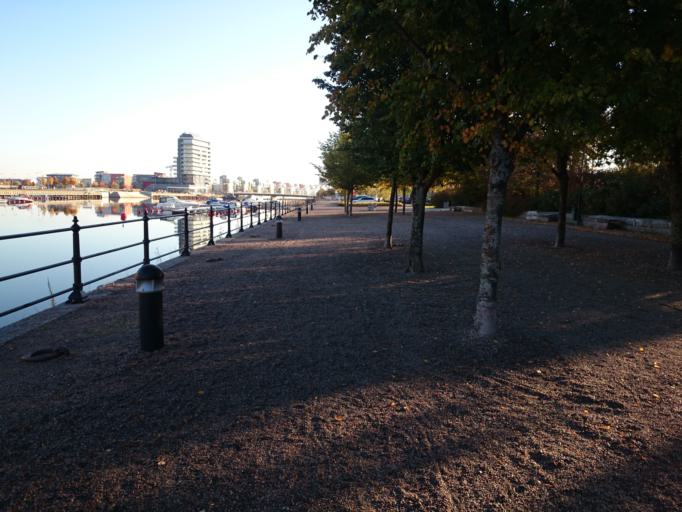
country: SE
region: Gaevleborg
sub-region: Gavle Kommun
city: Gavle
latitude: 60.6762
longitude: 17.1577
